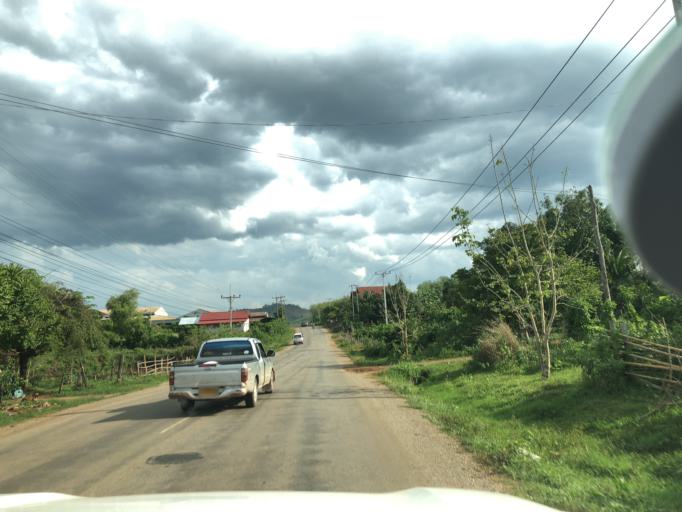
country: TH
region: Uttaradit
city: Ban Khok
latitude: 18.1492
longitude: 101.3823
